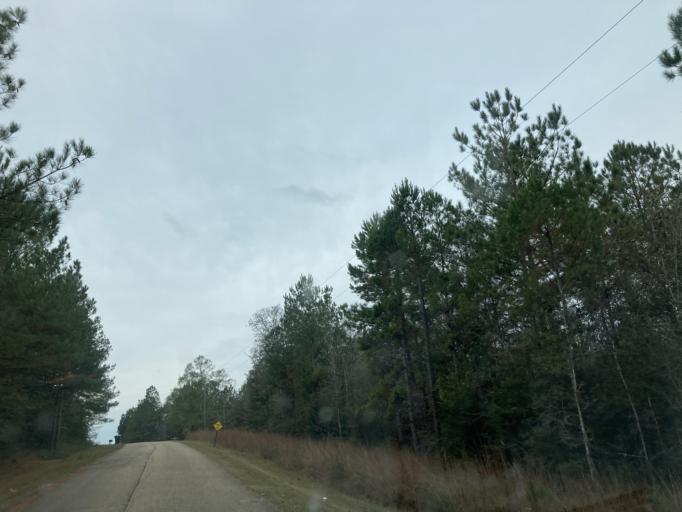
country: US
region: Mississippi
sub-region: Lamar County
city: Purvis
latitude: 31.1180
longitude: -89.4502
